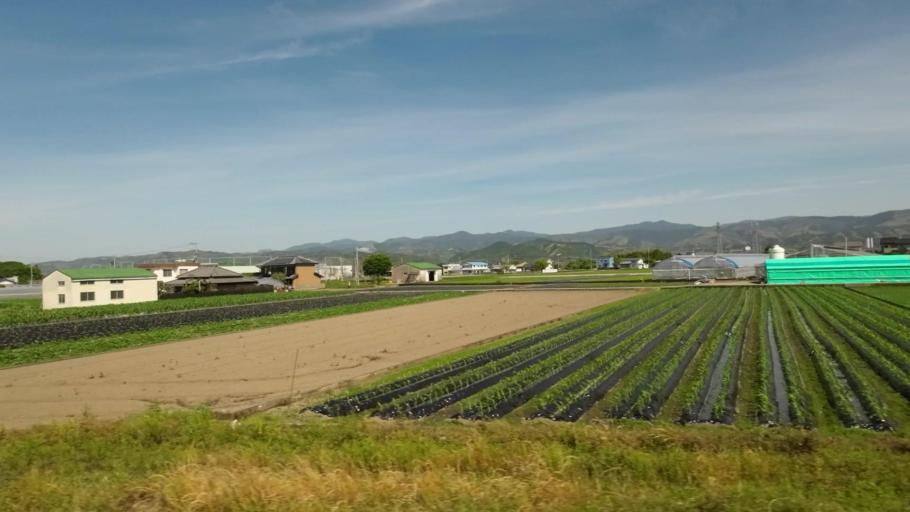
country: JP
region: Kochi
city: Kochi-shi
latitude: 33.5849
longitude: 133.6543
